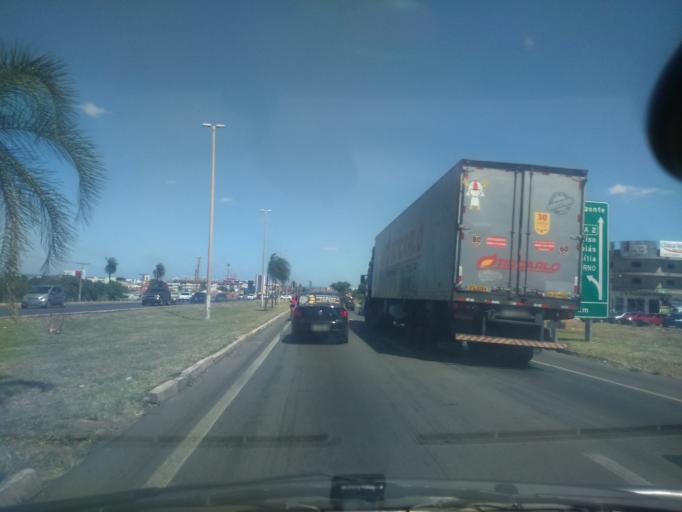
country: BR
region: Goias
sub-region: Luziania
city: Luziania
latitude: -16.0642
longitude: -47.9838
